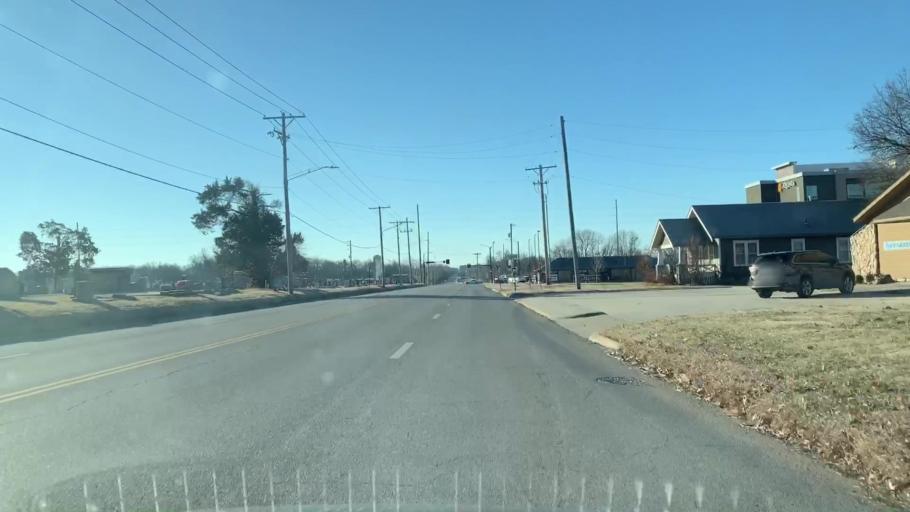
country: US
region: Kansas
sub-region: Crawford County
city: Pittsburg
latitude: 37.3838
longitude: -94.7053
